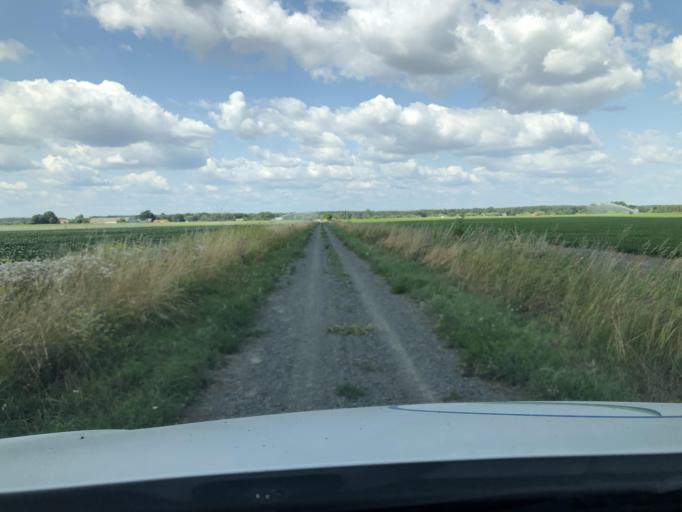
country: SE
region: Skane
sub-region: Kristianstads Kommun
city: Degeberga
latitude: 55.8874
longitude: 14.0812
